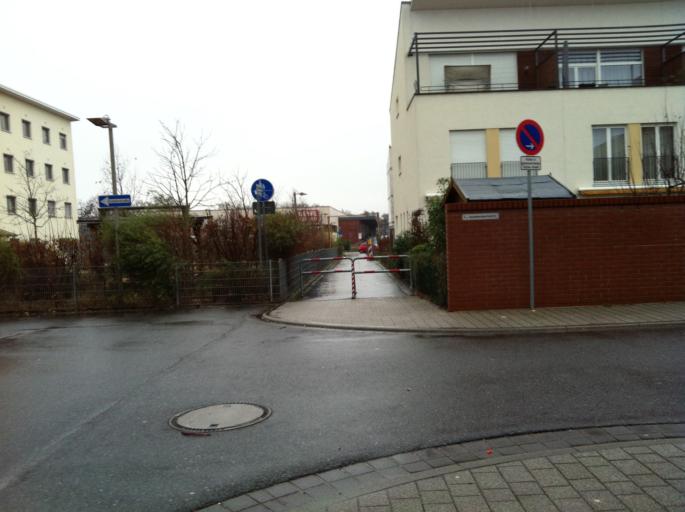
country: DE
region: Baden-Wuerttemberg
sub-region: Karlsruhe Region
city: Heidelberg
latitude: 49.3819
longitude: 8.6787
